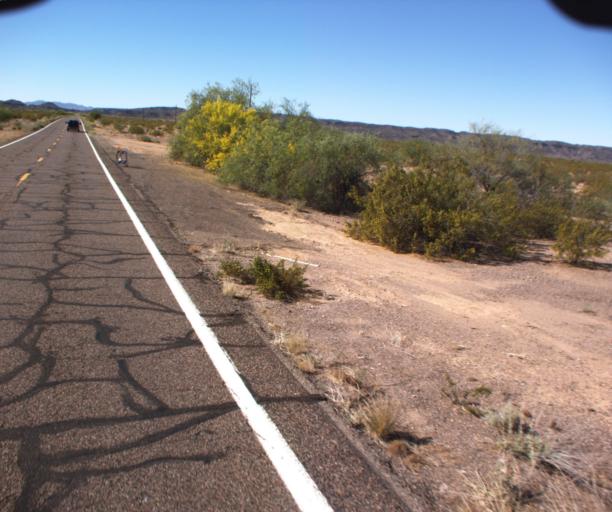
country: US
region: Arizona
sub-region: Pima County
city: Ajo
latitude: 32.6007
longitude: -112.8703
